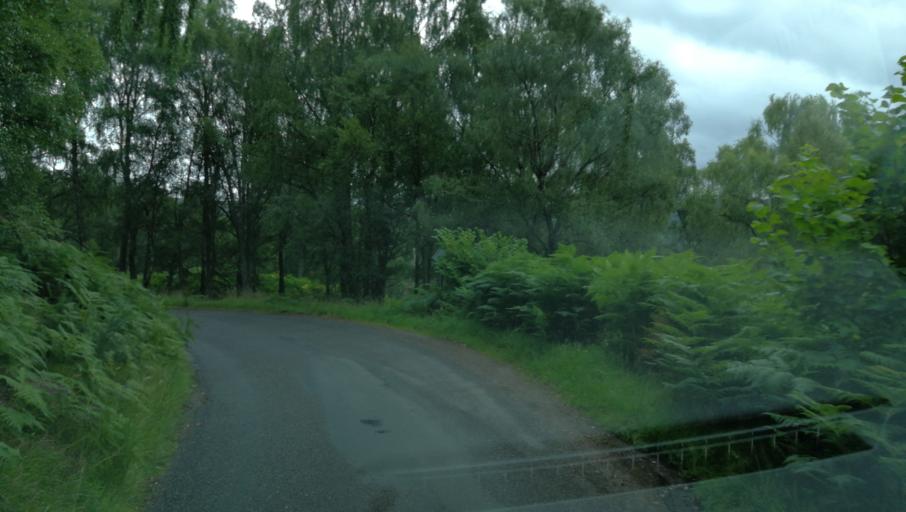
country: GB
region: Scotland
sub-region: Highland
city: Beauly
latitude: 57.3168
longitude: -4.8232
